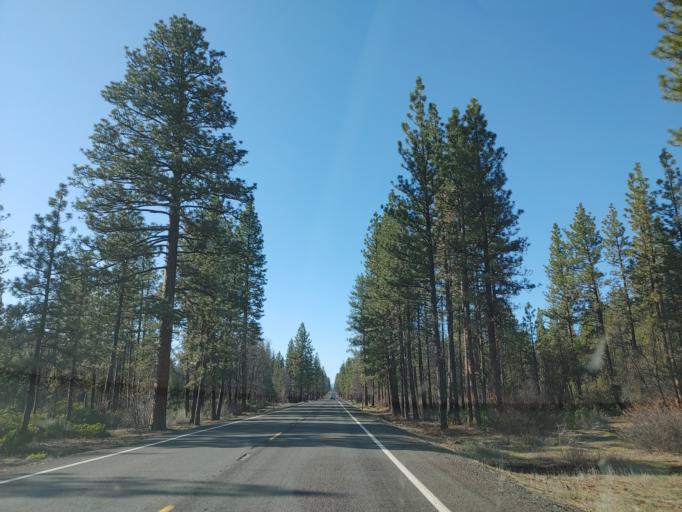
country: US
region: California
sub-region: Shasta County
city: Burney
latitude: 40.9215
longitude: -121.5965
